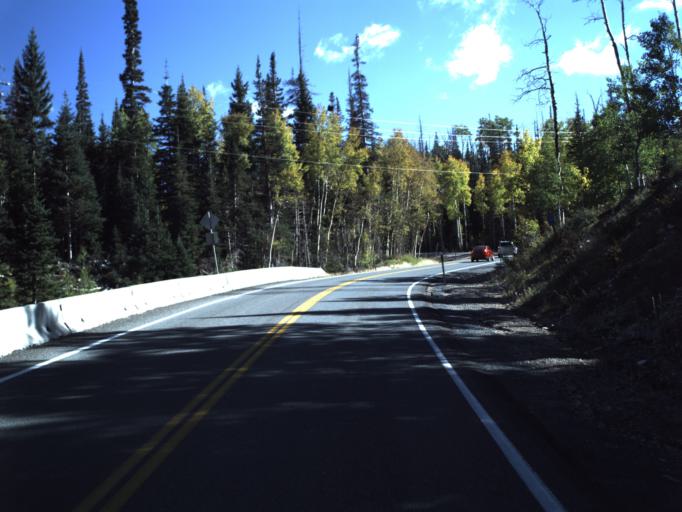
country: US
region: Utah
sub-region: Iron County
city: Parowan
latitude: 37.7107
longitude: -112.8519
